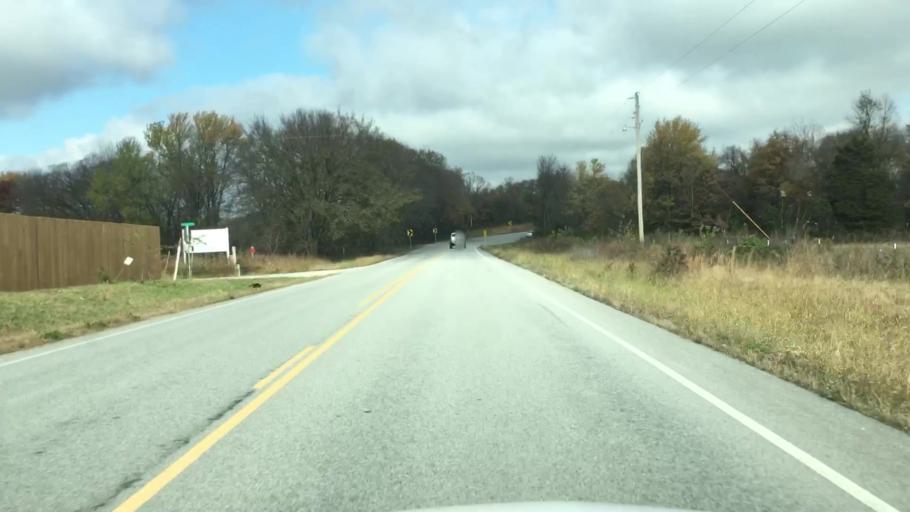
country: US
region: Arkansas
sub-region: Benton County
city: Centerton
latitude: 36.2919
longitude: -94.3454
